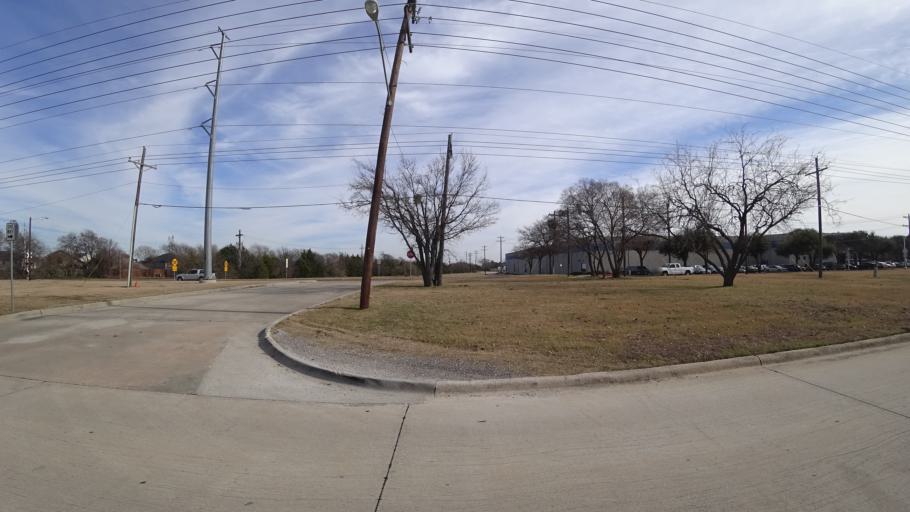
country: US
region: Texas
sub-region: Denton County
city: Highland Village
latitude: 33.0671
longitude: -97.0359
